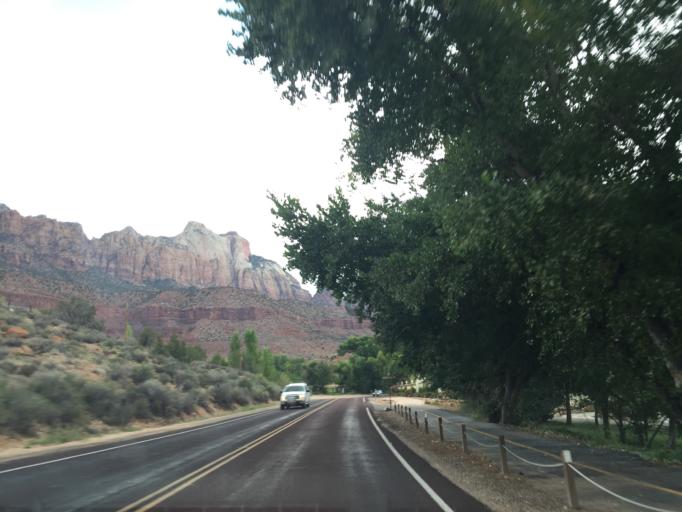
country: US
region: Utah
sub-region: Washington County
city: Hildale
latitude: 37.1718
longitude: -113.0135
